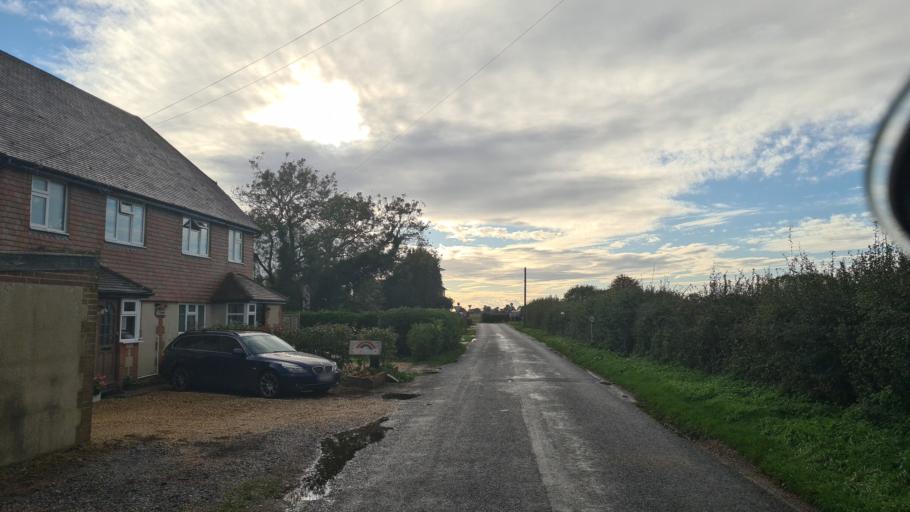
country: GB
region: England
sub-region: West Sussex
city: Walberton
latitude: 50.8111
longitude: -0.5898
